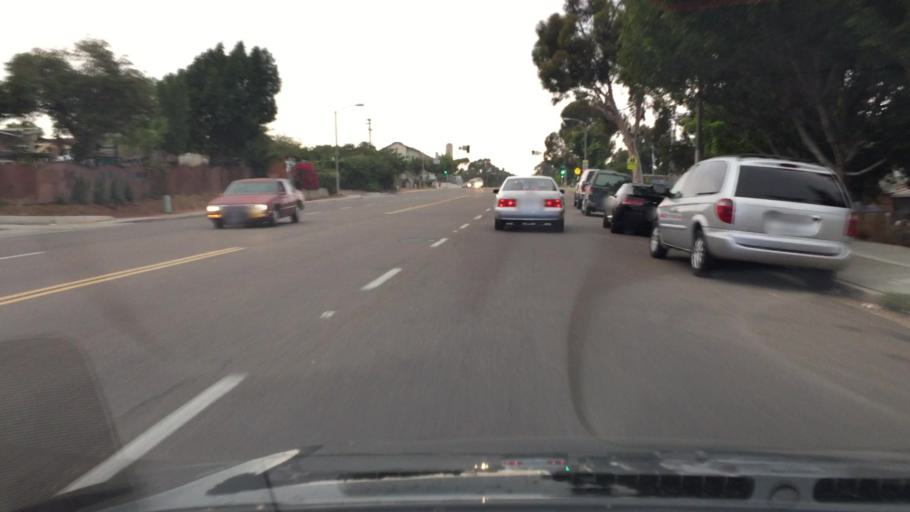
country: US
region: California
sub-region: San Diego County
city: National City
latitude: 32.7135
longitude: -117.0936
